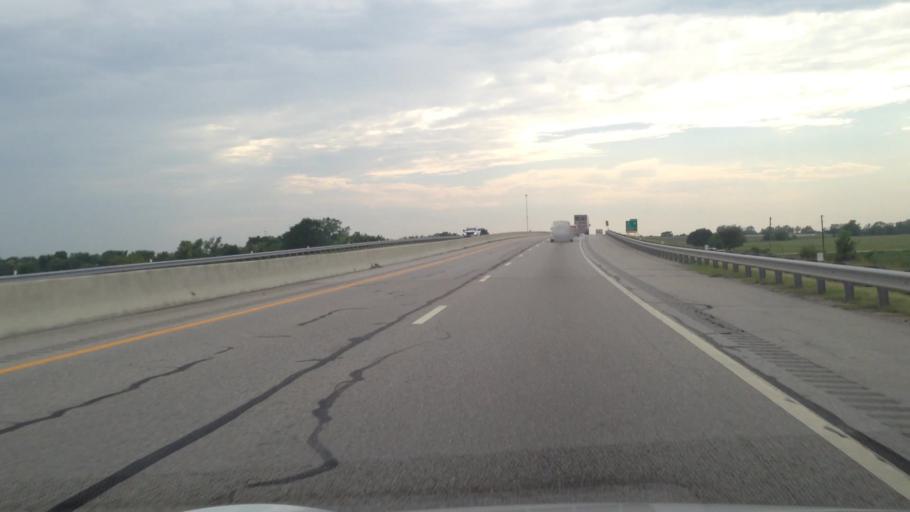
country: US
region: Oklahoma
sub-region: Ottawa County
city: Afton
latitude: 36.7264
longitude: -94.9245
